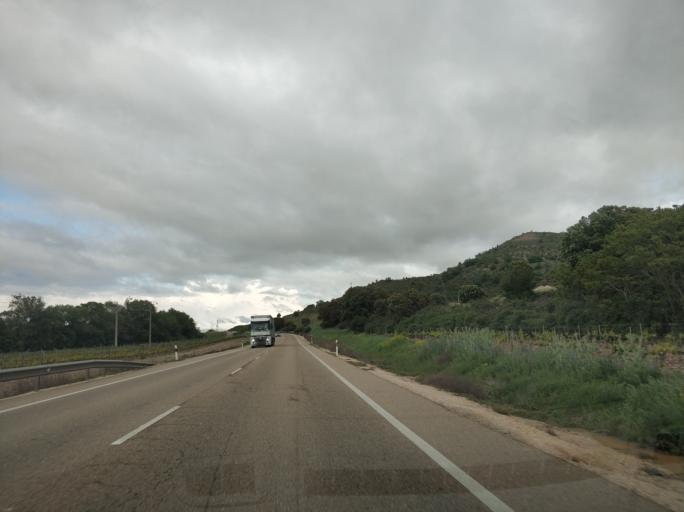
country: ES
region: Castille and Leon
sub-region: Provincia de Valladolid
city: Valbuena de Duero
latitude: 41.6259
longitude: -4.2784
